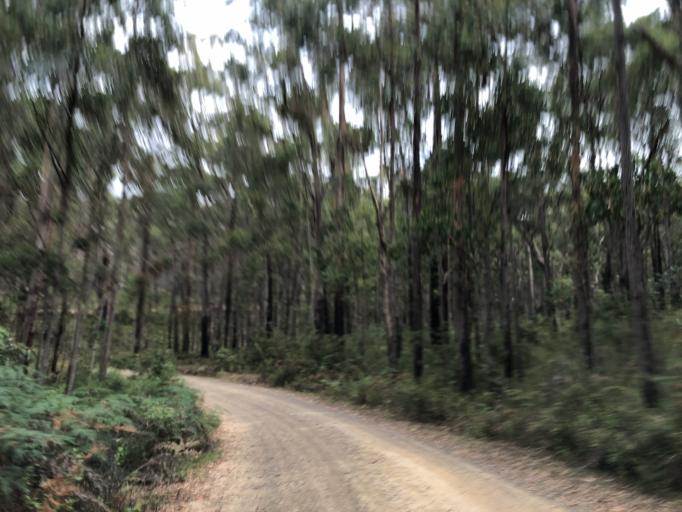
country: AU
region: Victoria
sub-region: Moorabool
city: Bacchus Marsh
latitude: -37.4728
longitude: 144.2820
